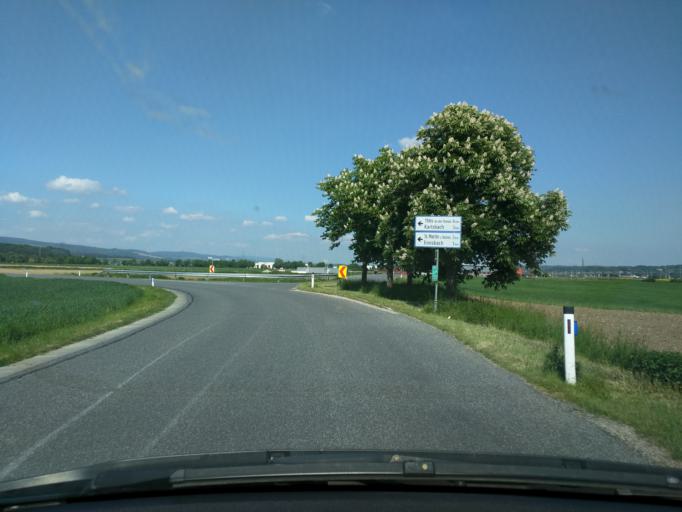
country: AT
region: Lower Austria
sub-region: Politischer Bezirk Melk
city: Neumarkt an der Ybbs
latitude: 48.1371
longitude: 15.0252
